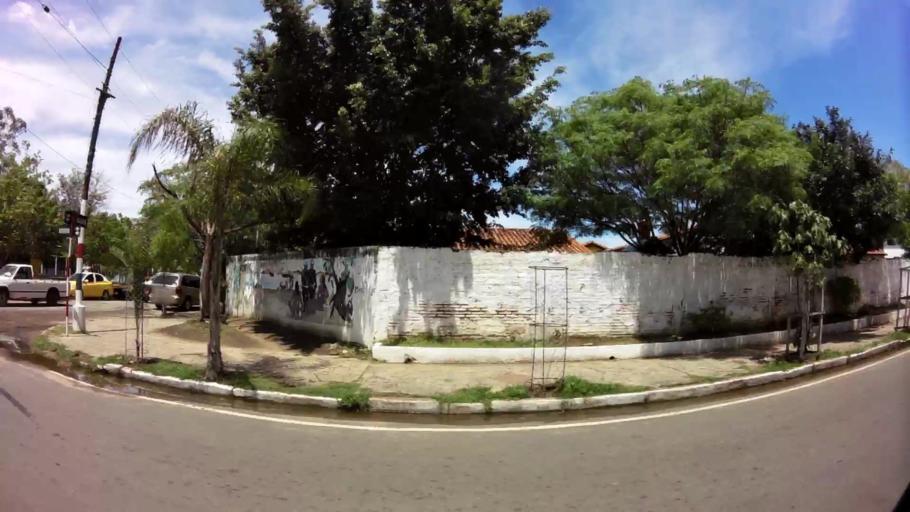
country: PY
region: Central
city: Colonia Mariano Roque Alonso
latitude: -25.2123
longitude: -57.5342
